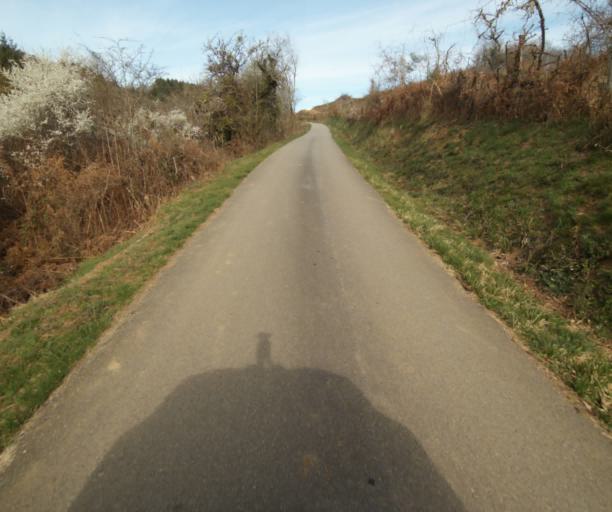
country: FR
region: Limousin
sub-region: Departement de la Correze
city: Correze
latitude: 45.4144
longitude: 1.7949
